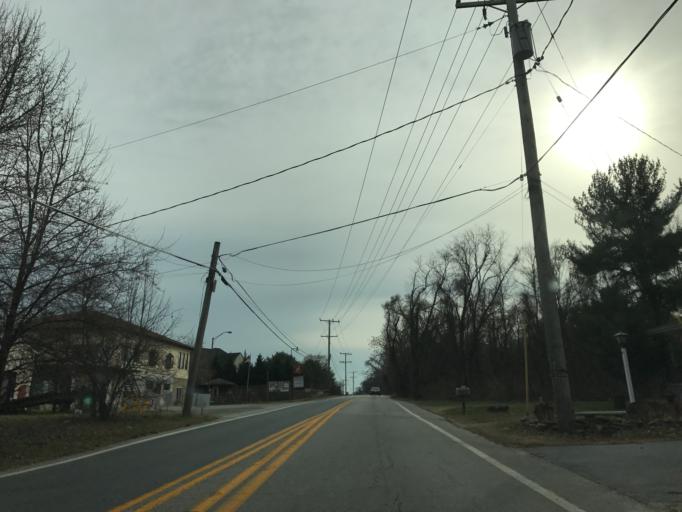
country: US
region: Maryland
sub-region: Anne Arundel County
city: Green Haven
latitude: 39.1303
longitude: -76.5630
